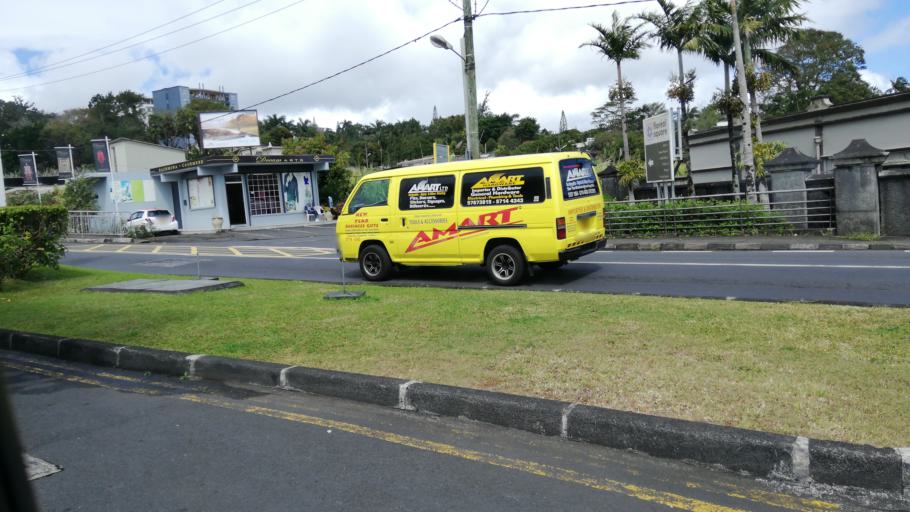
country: MU
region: Plaines Wilhems
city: Curepipe
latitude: -20.3076
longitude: 57.5083
